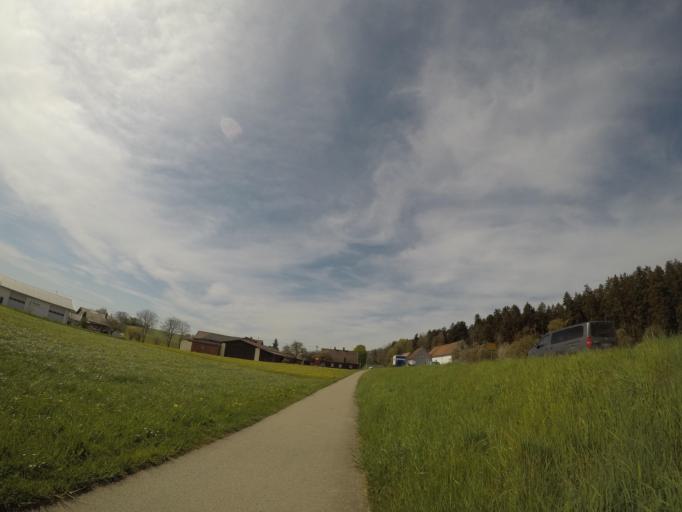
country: DE
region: Baden-Wuerttemberg
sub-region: Tuebingen Region
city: Boms
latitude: 47.9780
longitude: 9.5116
